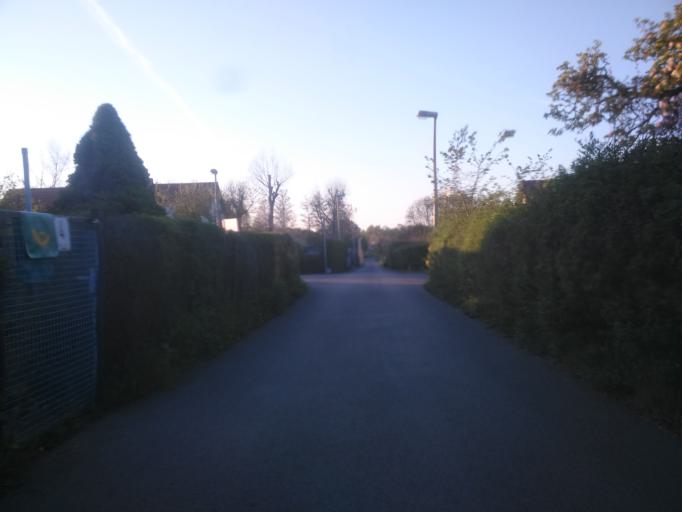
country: DE
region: Berlin
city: Stadtrandsiedlung Malchow
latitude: 52.5730
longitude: 13.4707
